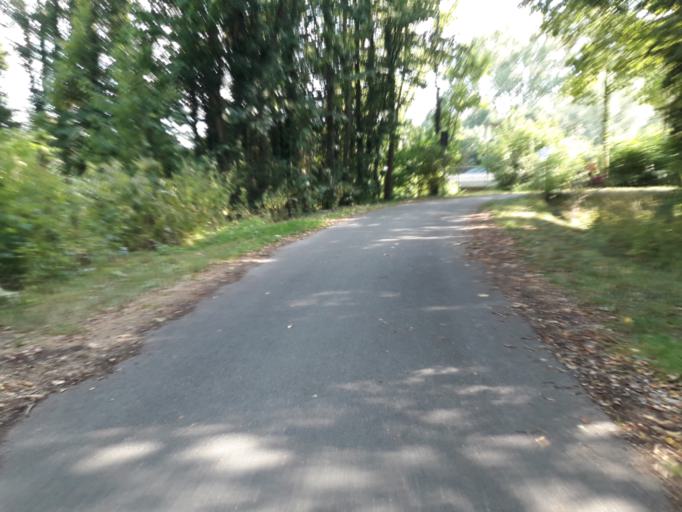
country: DE
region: North Rhine-Westphalia
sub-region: Regierungsbezirk Detmold
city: Paderborn
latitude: 51.7076
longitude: 8.7106
